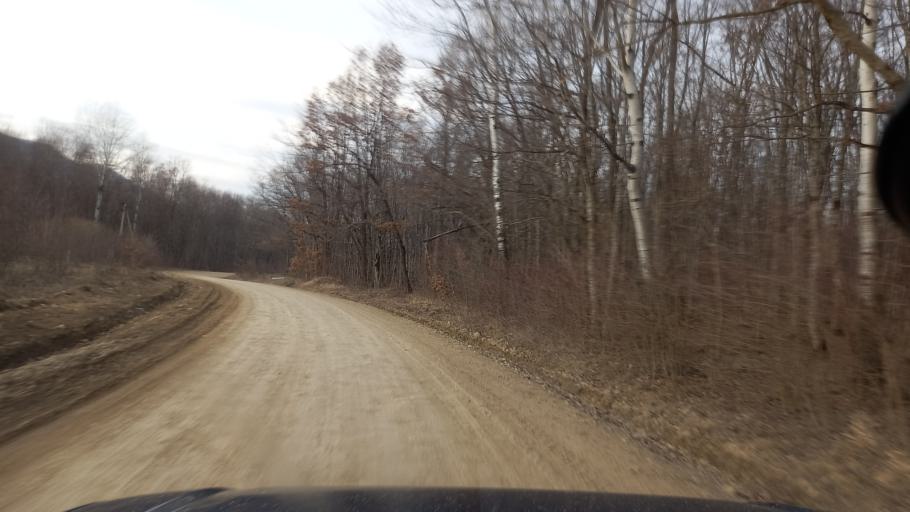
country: RU
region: Adygeya
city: Kamennomostskiy
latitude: 44.1616
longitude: 40.2451
